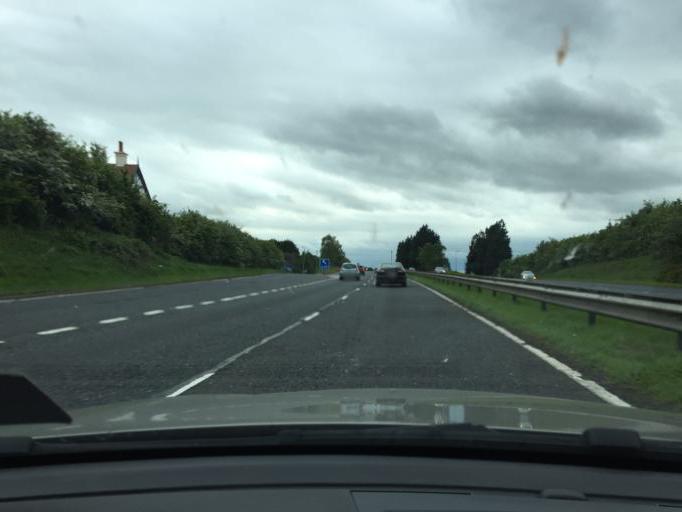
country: GB
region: Northern Ireland
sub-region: Lisburn District
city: Lisburn
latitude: 54.5083
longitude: -6.0251
